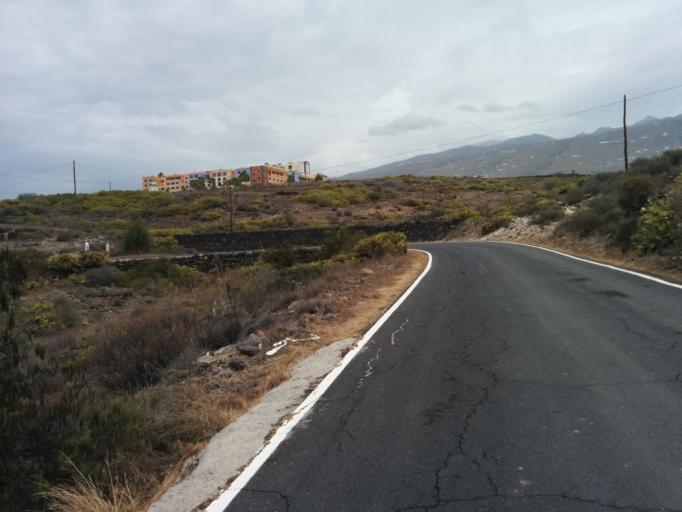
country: ES
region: Canary Islands
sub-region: Provincia de Santa Cruz de Tenerife
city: Adeje
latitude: 28.1155
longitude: -16.7693
